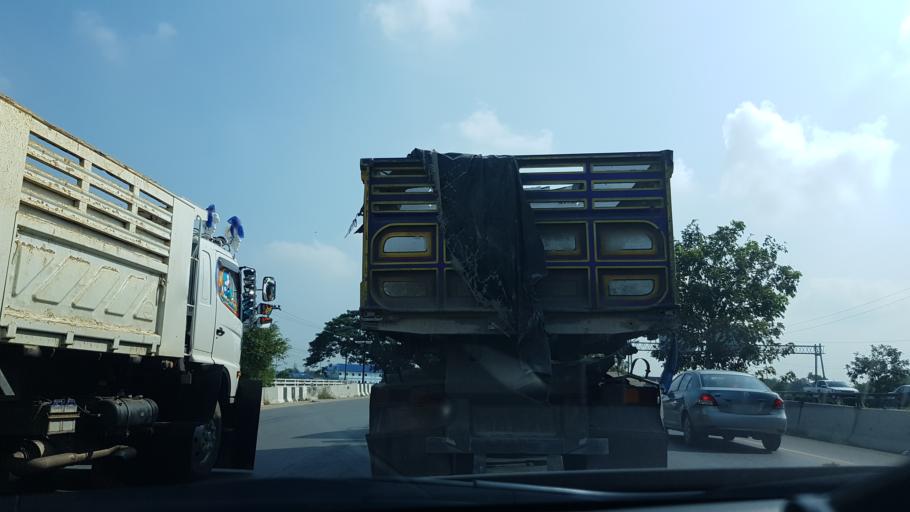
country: TH
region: Phra Nakhon Si Ayutthaya
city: Bang Pa-in
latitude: 14.1587
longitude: 100.5711
